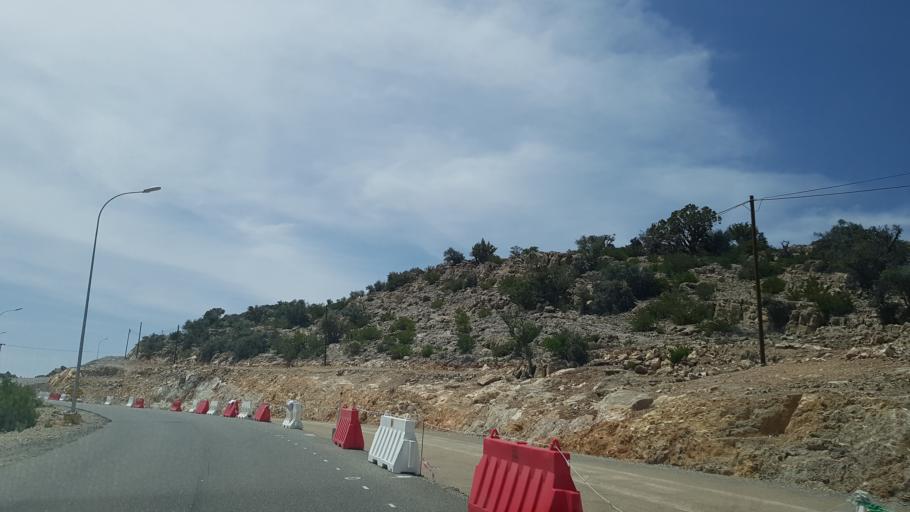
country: OM
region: Muhafazat ad Dakhiliyah
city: Nizwa
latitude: 23.1160
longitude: 57.6412
